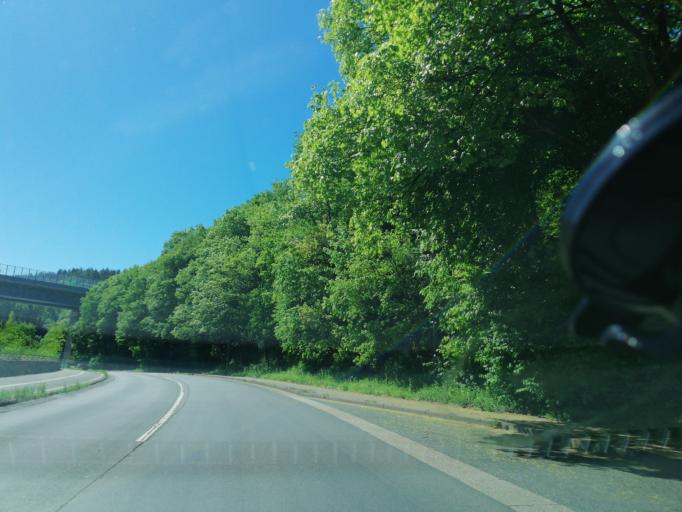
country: DE
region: North Rhine-Westphalia
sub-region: Regierungsbezirk Dusseldorf
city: Wuppertal
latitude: 51.2585
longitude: 7.2297
